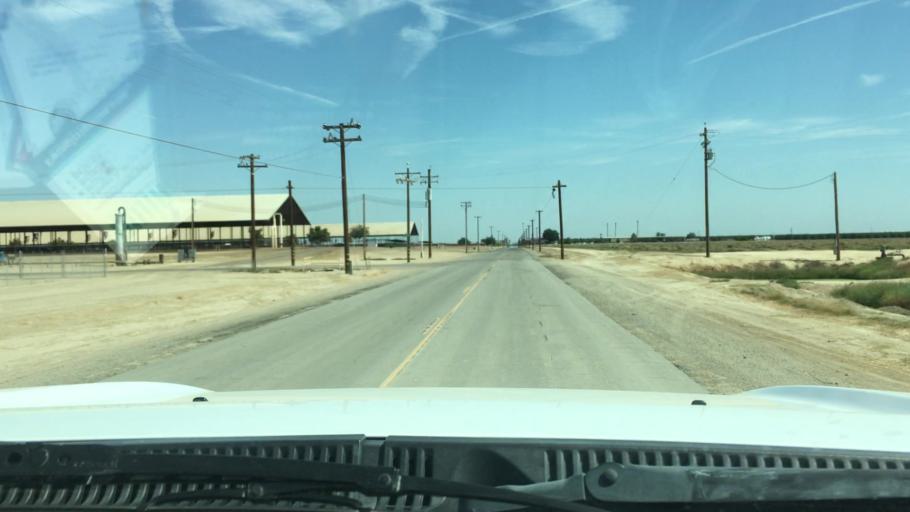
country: US
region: California
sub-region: Kern County
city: Buttonwillow
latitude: 35.4125
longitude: -119.3765
